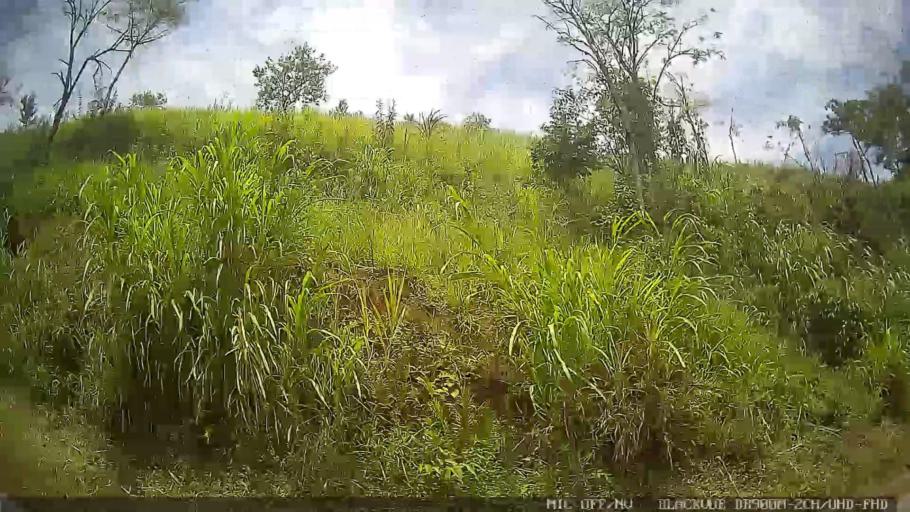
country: BR
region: Sao Paulo
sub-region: Santa Isabel
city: Santa Isabel
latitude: -23.3318
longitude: -46.2173
